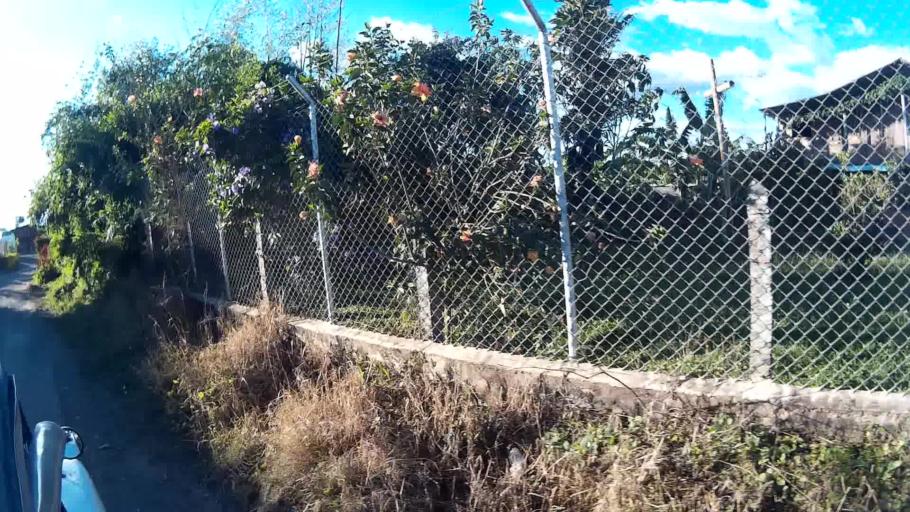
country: CO
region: Quindio
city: Filandia
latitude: 4.7227
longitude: -75.6792
